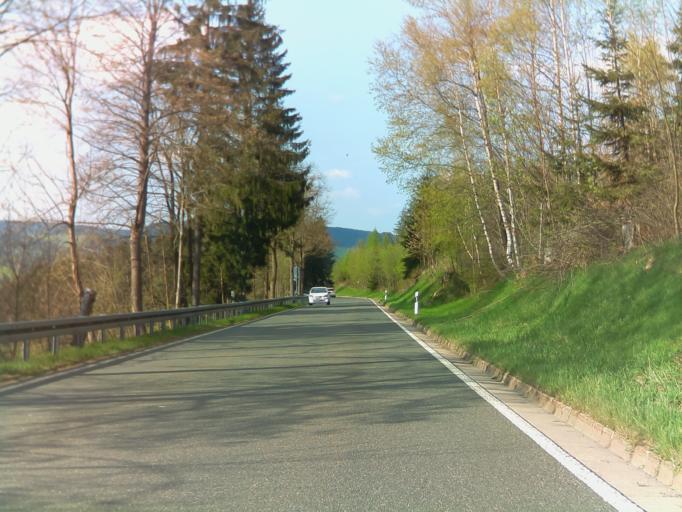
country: DE
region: Thuringia
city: Grafenthal
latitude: 50.5003
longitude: 11.2892
